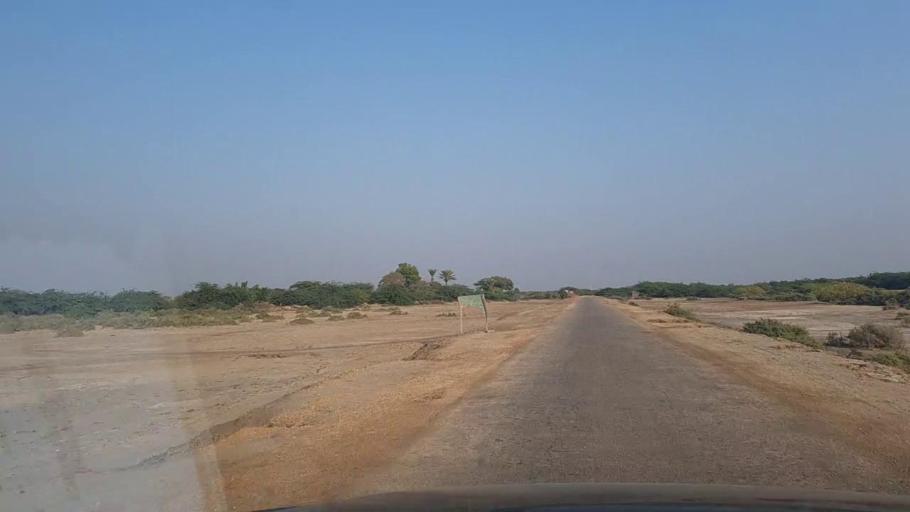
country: PK
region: Sindh
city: Keti Bandar
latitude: 24.2655
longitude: 67.5587
